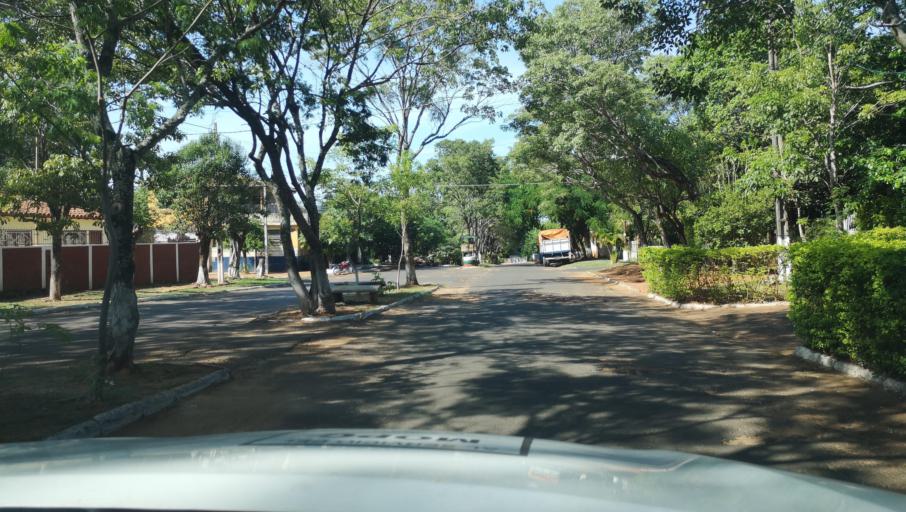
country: PY
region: Misiones
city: Santa Maria
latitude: -26.8928
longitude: -57.0195
